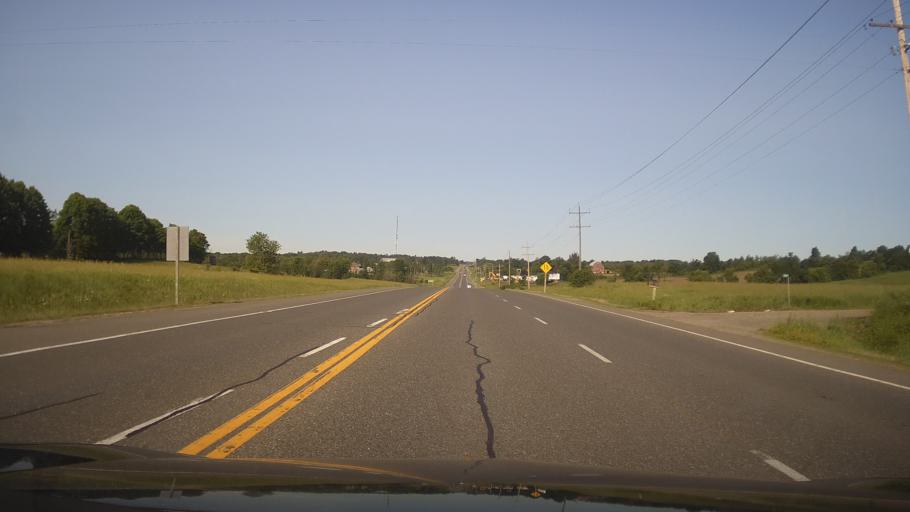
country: CA
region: Ontario
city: Peterborough
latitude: 44.3606
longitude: -78.0250
